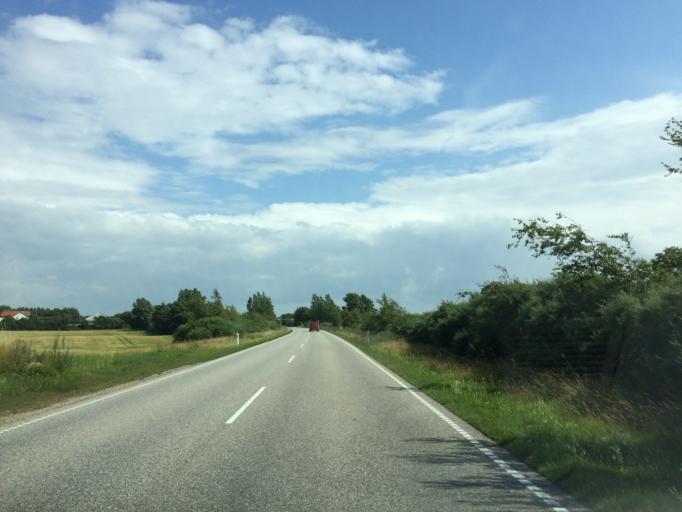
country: DK
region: Zealand
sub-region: Odsherred Kommune
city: Asnaes
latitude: 55.9657
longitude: 11.3612
